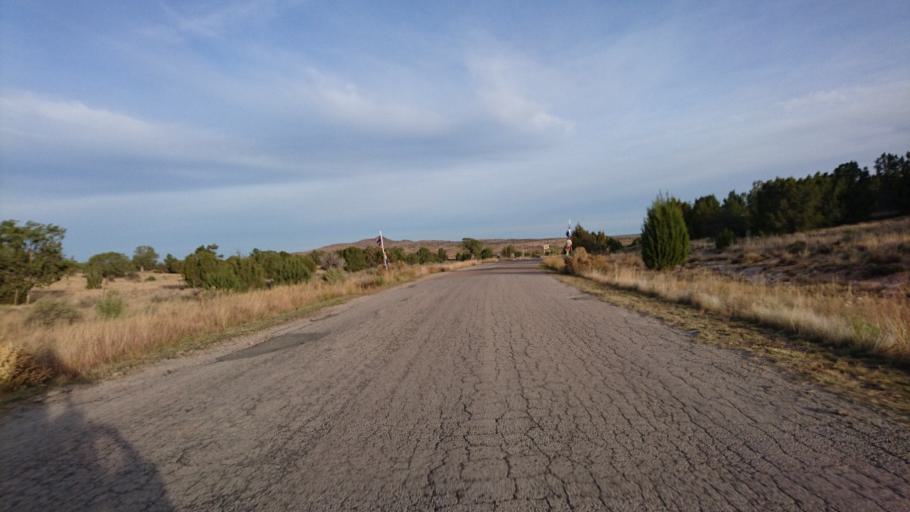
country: US
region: Arizona
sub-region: Mohave County
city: Peach Springs
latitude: 35.5228
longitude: -113.2273
